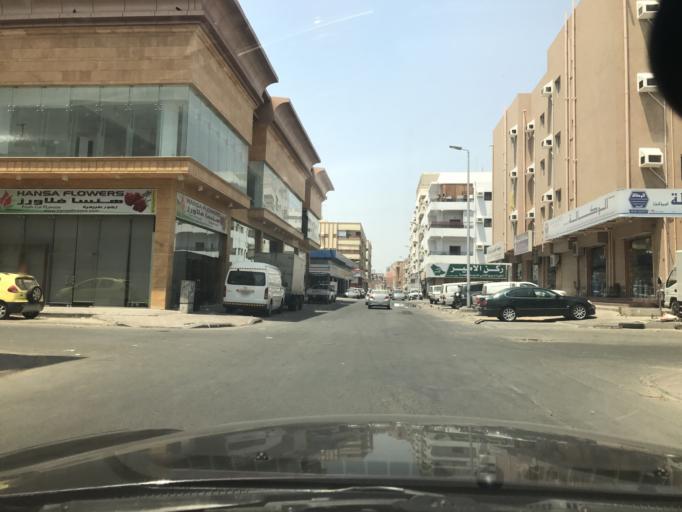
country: SA
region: Makkah
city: Jeddah
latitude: 21.4698
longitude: 39.1855
